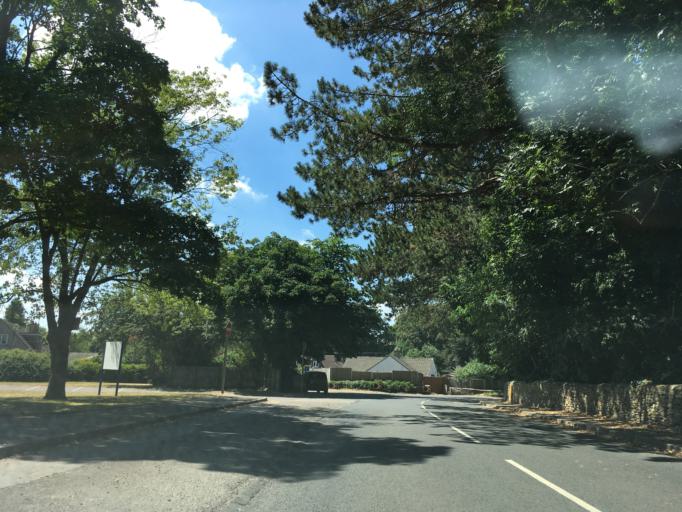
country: GB
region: England
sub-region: Gloucestershire
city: Chalford
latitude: 51.7357
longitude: -2.1594
